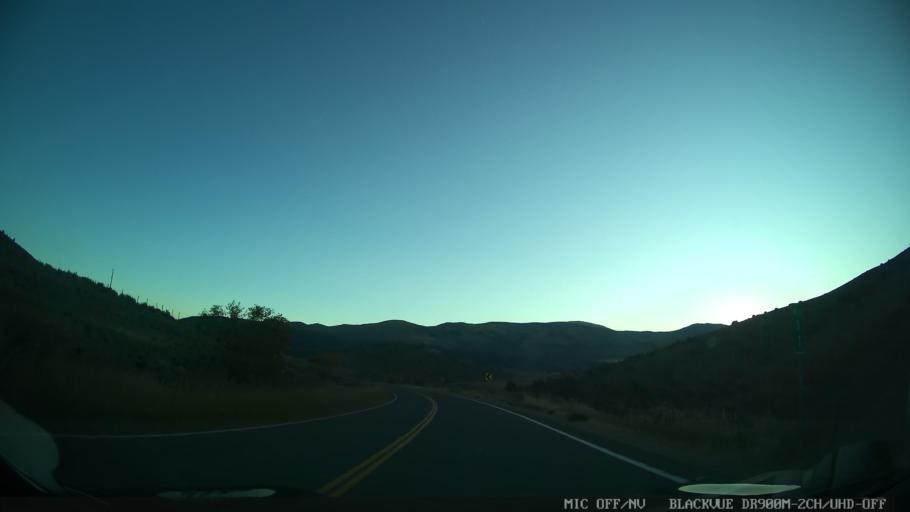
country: US
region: Colorado
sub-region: Eagle County
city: Edwards
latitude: 39.8221
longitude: -106.6447
